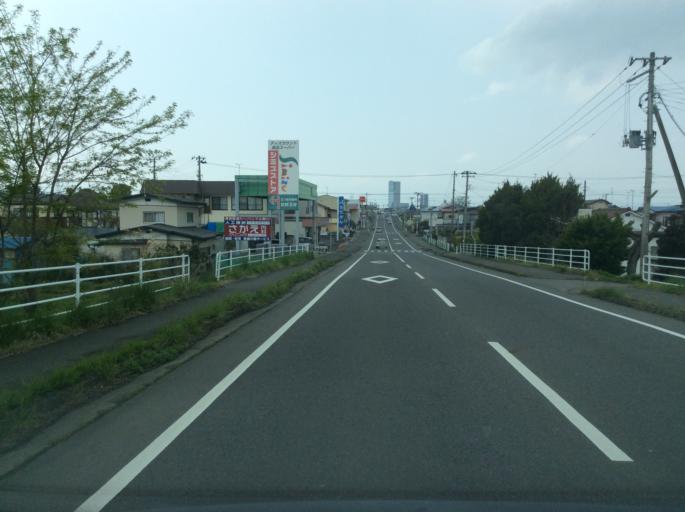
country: JP
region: Fukushima
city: Koriyama
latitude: 37.3832
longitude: 140.4049
